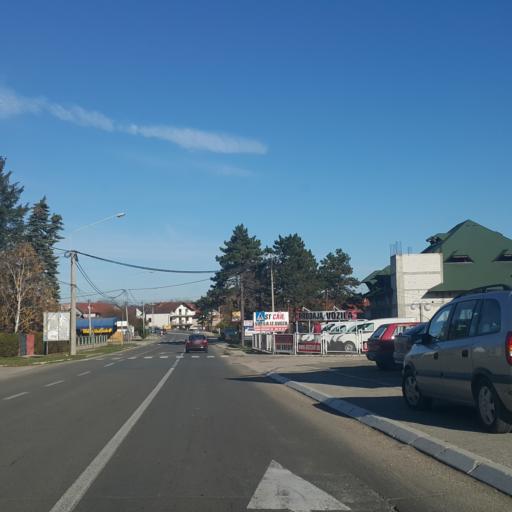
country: RS
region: Central Serbia
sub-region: Sumadijski Okrug
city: Topola
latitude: 44.2585
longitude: 20.6837
